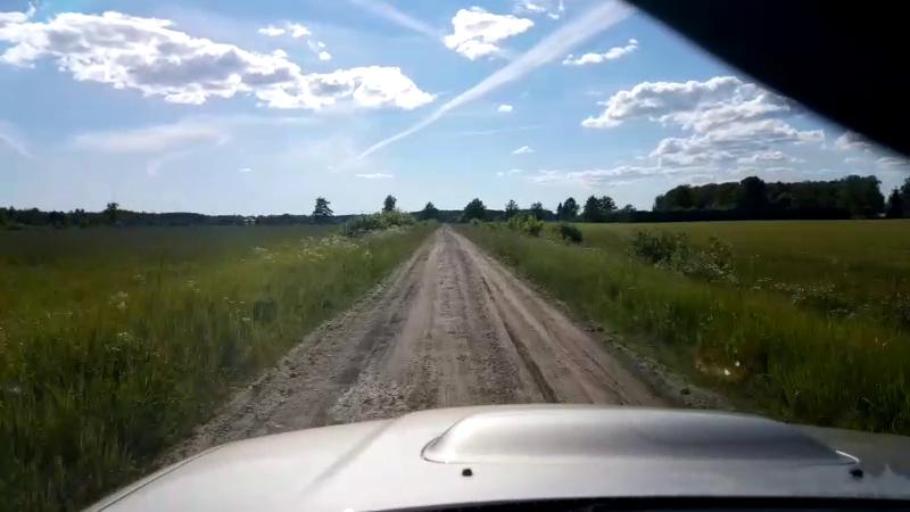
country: EE
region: Paernumaa
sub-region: Sauga vald
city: Sauga
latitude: 58.4916
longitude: 24.5697
